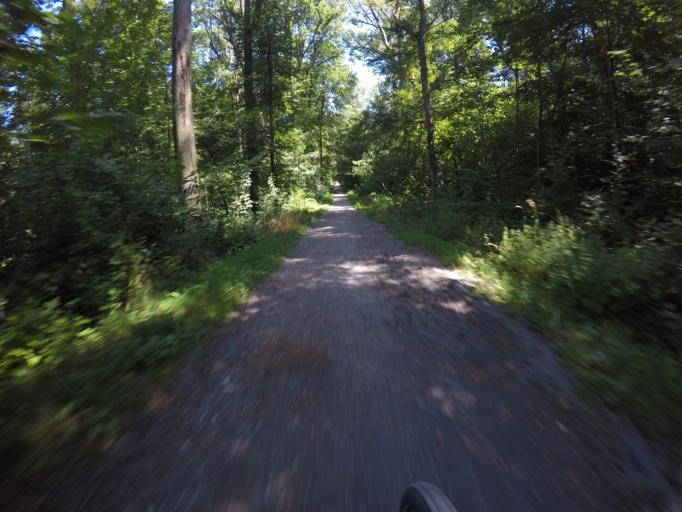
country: DE
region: Baden-Wuerttemberg
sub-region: Regierungsbezirk Stuttgart
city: Leinfelden-Echterdingen
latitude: 48.7103
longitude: 9.1798
